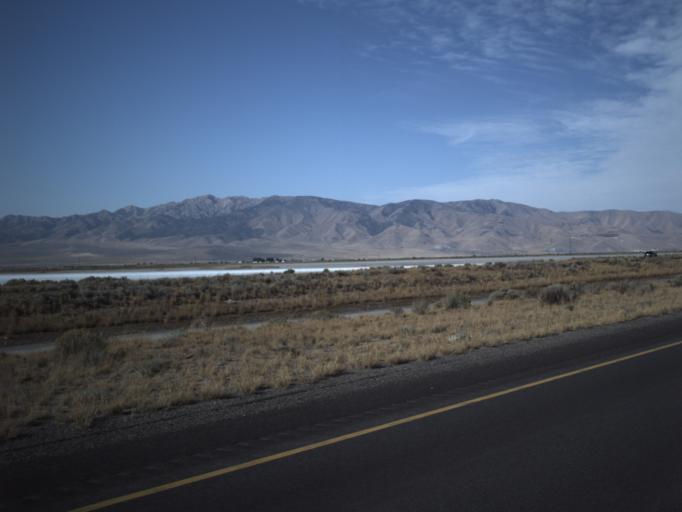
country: US
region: Utah
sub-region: Tooele County
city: Grantsville
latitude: 40.6764
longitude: -112.4036
